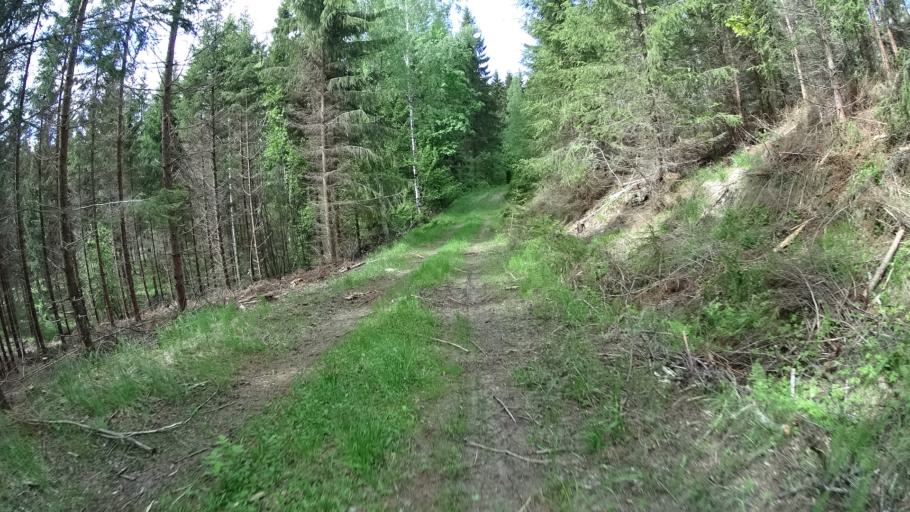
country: FI
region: Uusimaa
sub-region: Raaseporin
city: Pohja
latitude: 60.1635
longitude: 23.6066
